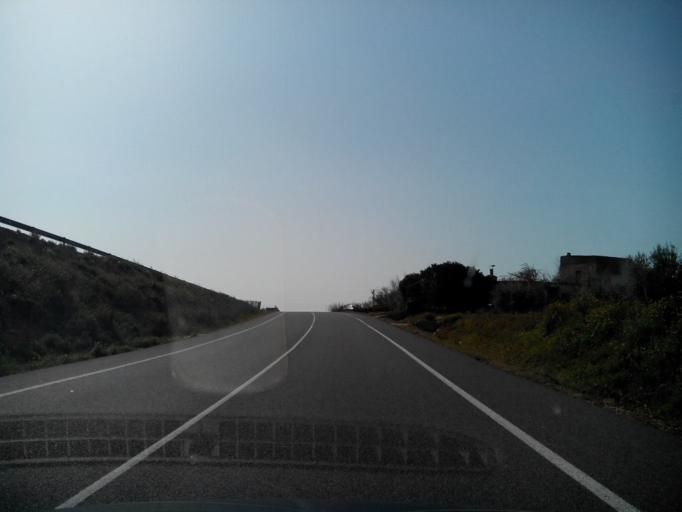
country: ES
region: Catalonia
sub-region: Provincia de Tarragona
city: Alcover
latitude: 41.2605
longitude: 1.1761
